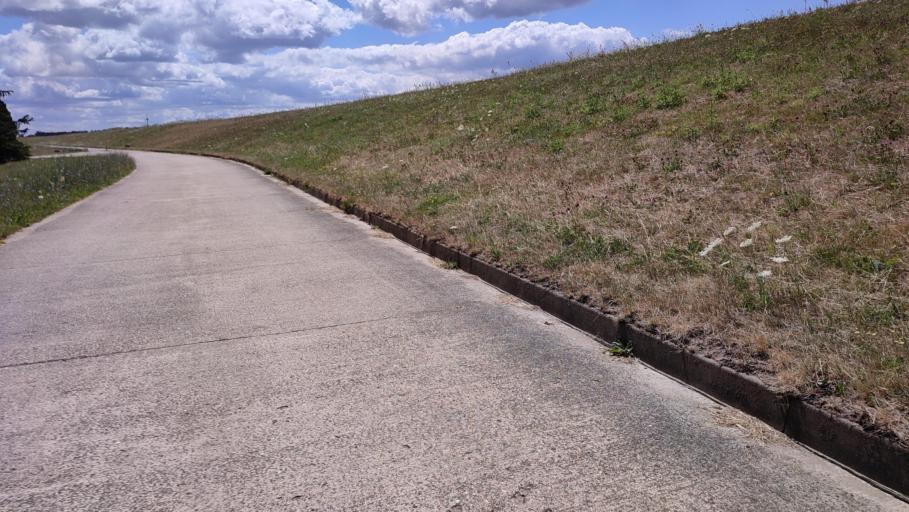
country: DE
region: Lower Saxony
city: Hitzacker
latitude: 53.1951
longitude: 10.9838
